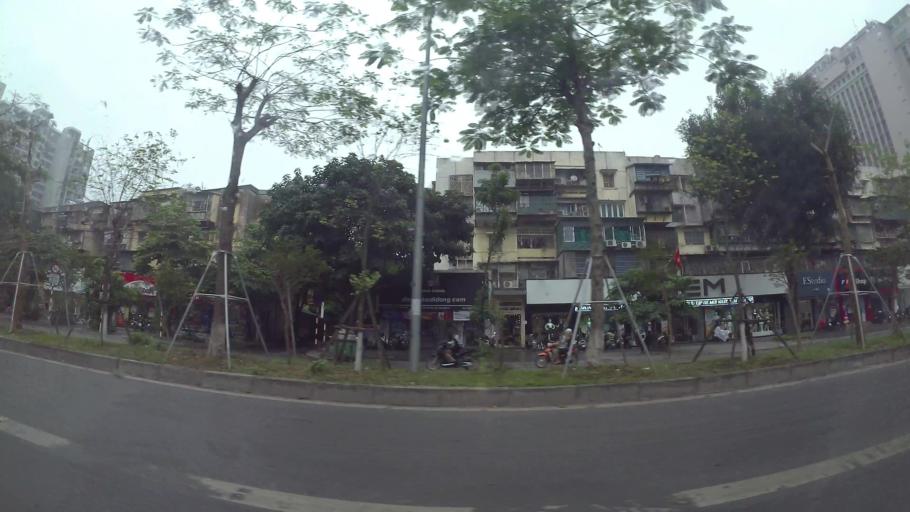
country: VN
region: Ha Noi
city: Dong Da
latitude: 21.0204
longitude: 105.8177
